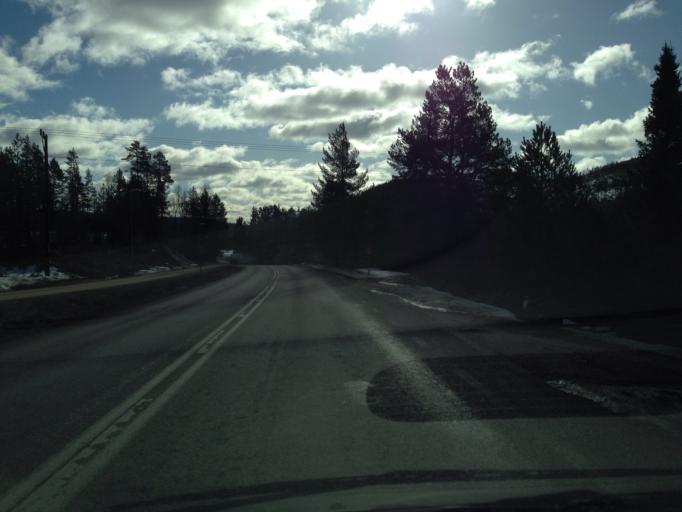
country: SE
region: Gaevleborg
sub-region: Ljusdals Kommun
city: Farila
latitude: 61.9820
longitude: 15.3155
